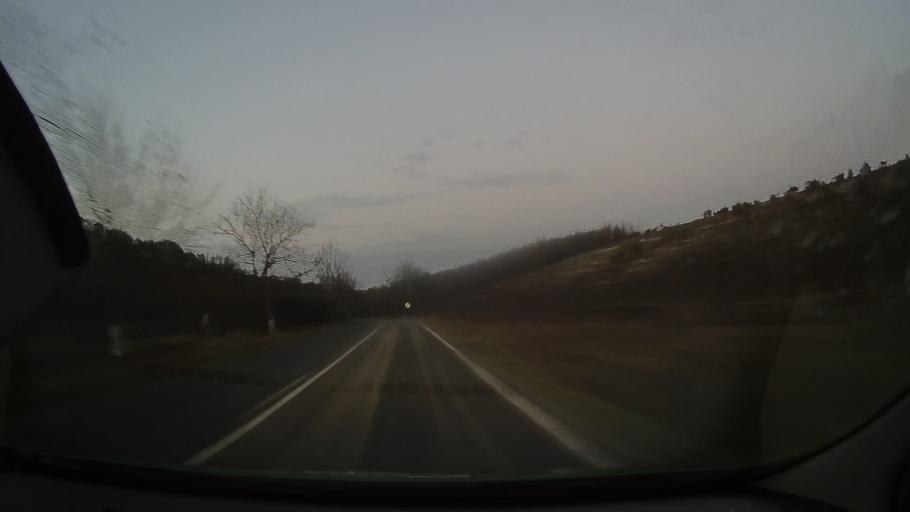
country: RO
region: Constanta
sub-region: Comuna Baneasa
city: Baneasa
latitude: 44.0765
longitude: 27.7380
